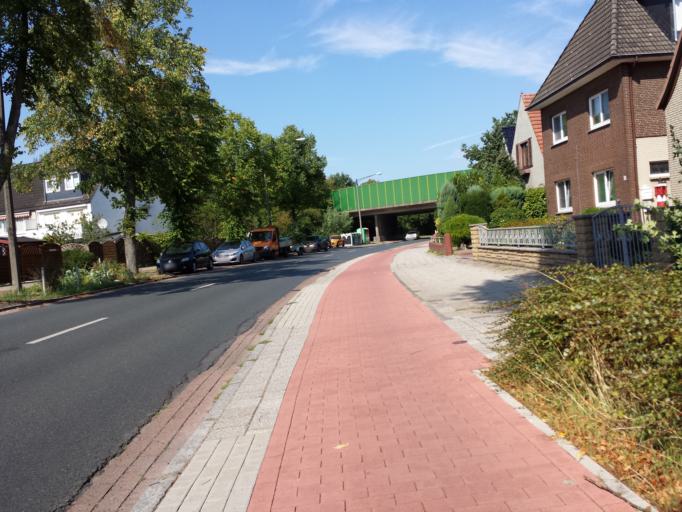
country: DE
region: Bremen
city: Bremen
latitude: 53.0342
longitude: 8.8513
